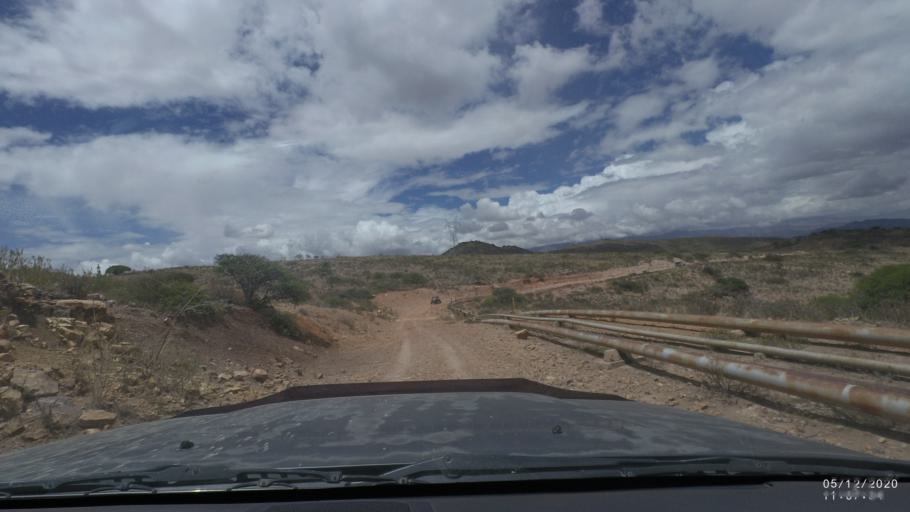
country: BO
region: Cochabamba
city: Sipe Sipe
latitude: -17.5518
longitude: -66.3093
